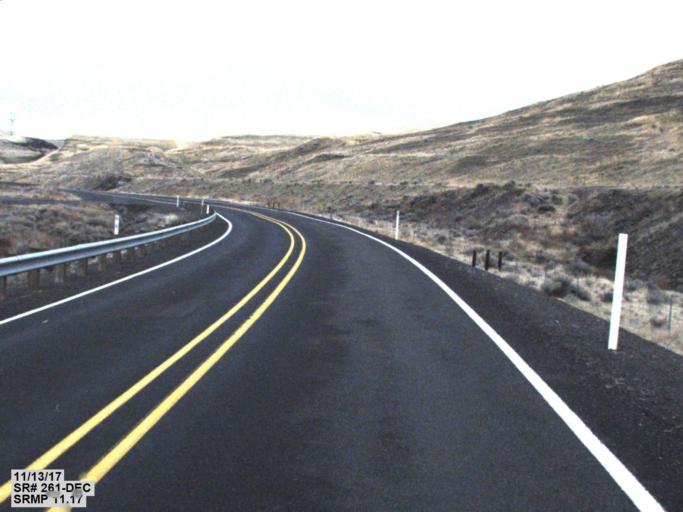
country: US
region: Washington
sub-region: Walla Walla County
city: Waitsburg
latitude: 46.5474
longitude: -118.1781
